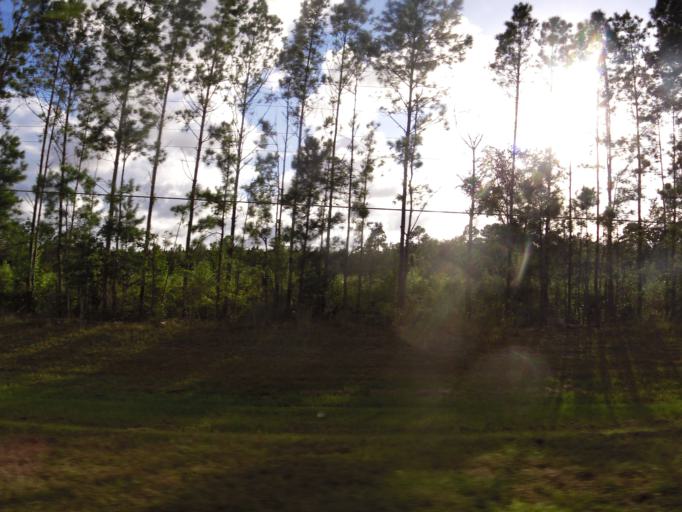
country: US
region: Georgia
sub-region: Liberty County
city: Midway
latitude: 31.7290
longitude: -81.4263
